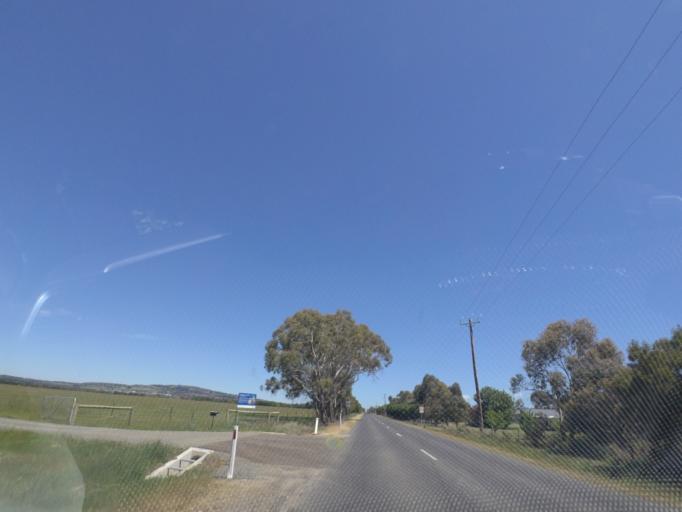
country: AU
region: Victoria
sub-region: Hume
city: Sunbury
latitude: -37.4749
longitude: 144.6183
